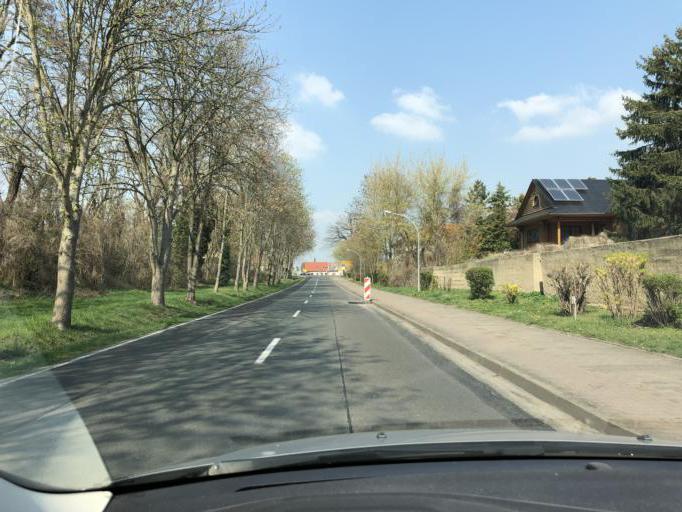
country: DE
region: Saxony-Anhalt
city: Zorbig
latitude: 51.6267
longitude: 12.1230
